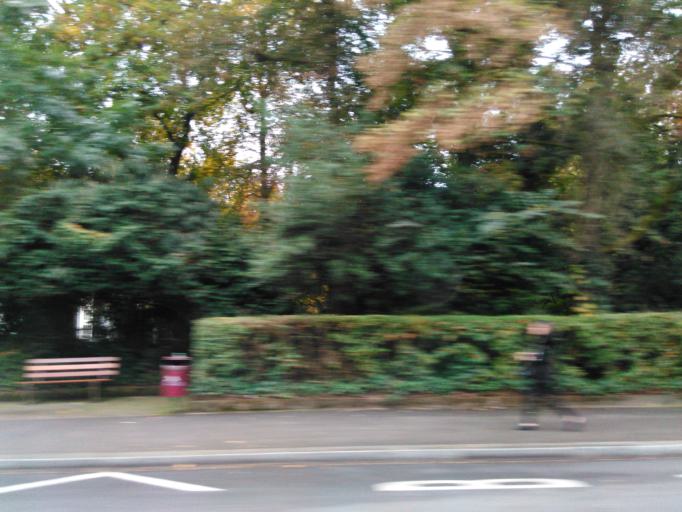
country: LU
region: Luxembourg
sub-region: Canton de Luxembourg
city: Luxembourg
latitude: 49.6124
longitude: 6.1239
